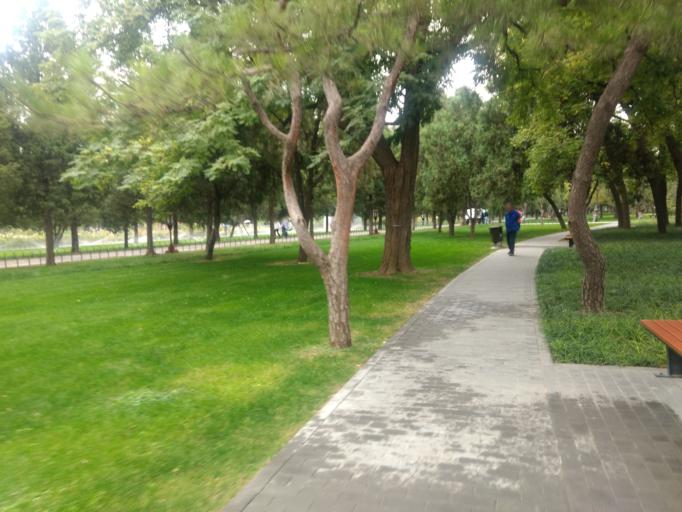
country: CN
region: Beijing
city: Longtan
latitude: 39.8814
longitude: 116.4024
